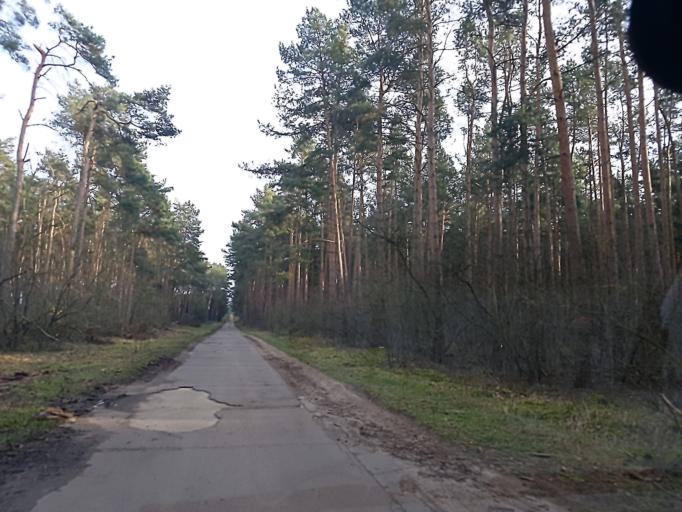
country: DE
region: Brandenburg
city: Wollin
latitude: 52.2725
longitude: 12.4867
